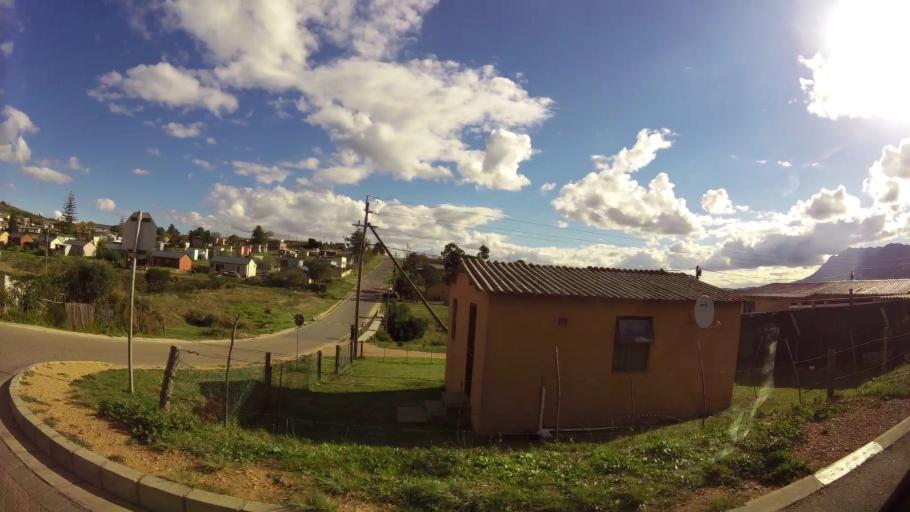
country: ZA
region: Western Cape
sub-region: Overberg District Municipality
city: Swellendam
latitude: -34.0319
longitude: 20.4492
